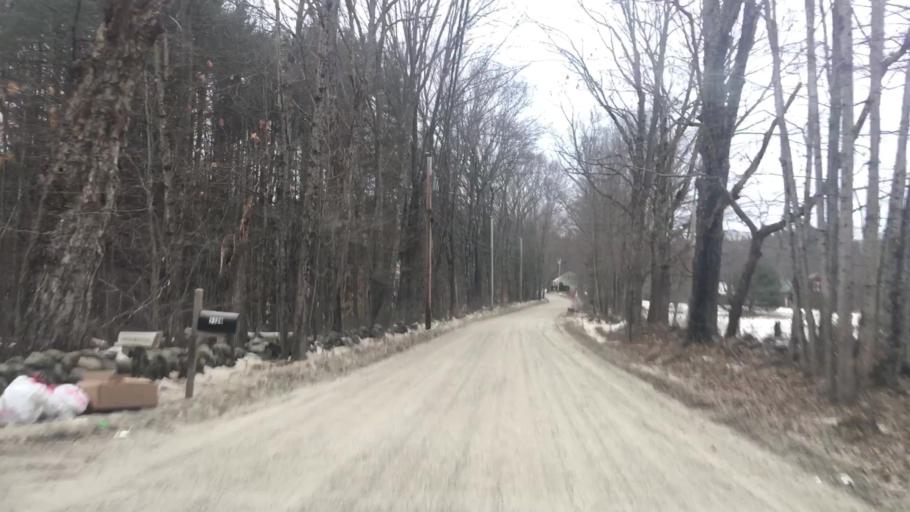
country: US
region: New Hampshire
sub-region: Merrimack County
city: Hopkinton
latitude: 43.1621
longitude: -71.6677
